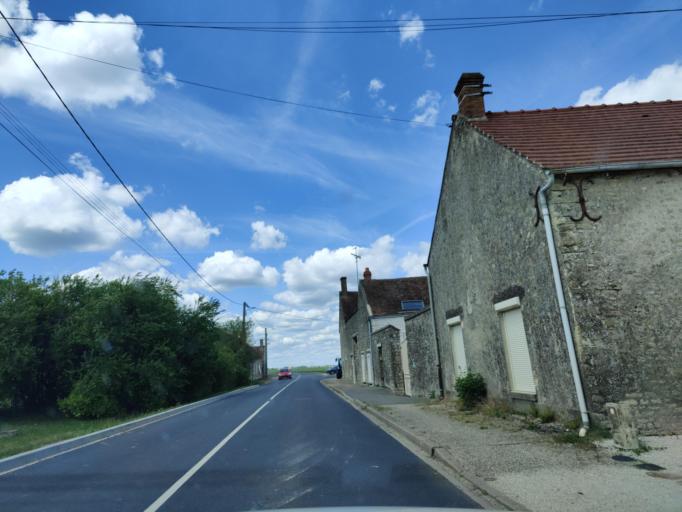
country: FR
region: Centre
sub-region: Departement du Loiret
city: Dadonville
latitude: 48.1028
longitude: 2.2688
